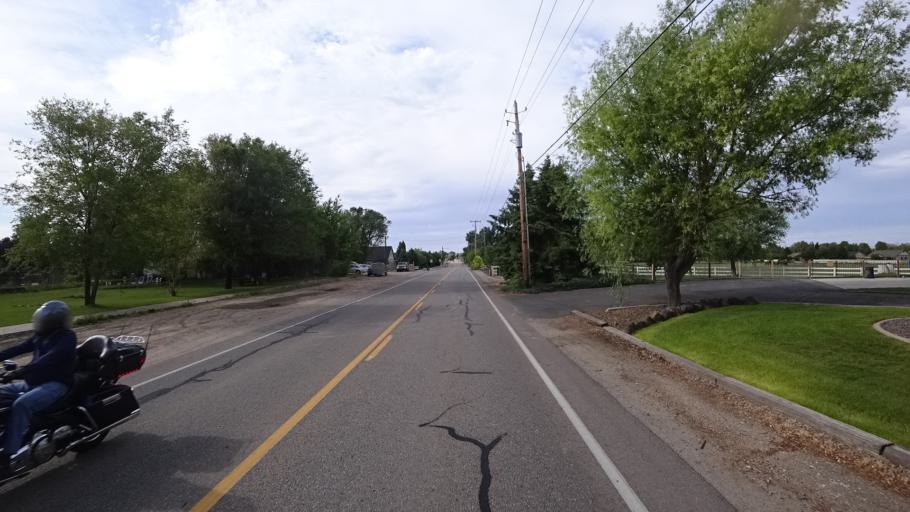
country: US
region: Idaho
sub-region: Ada County
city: Meridian
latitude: 43.5780
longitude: -116.3747
